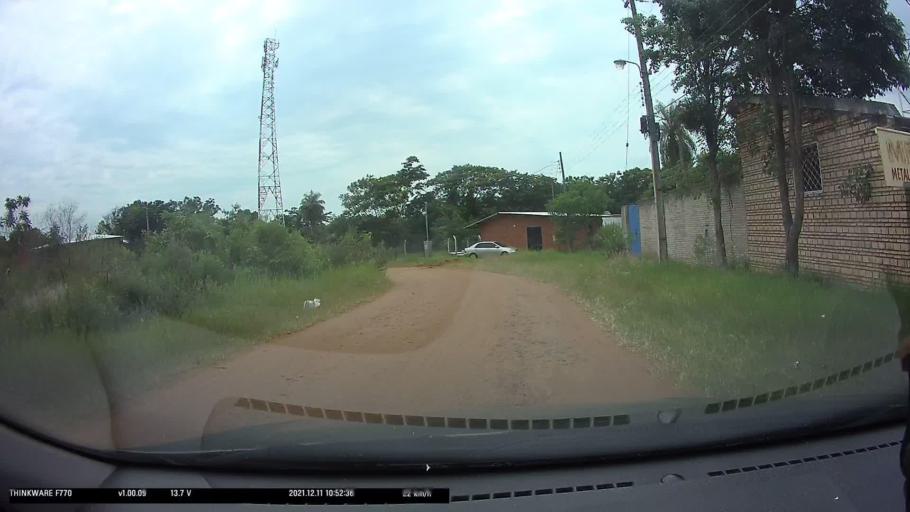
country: PY
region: Cordillera
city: San Bernardino
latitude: -25.2930
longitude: -57.2684
